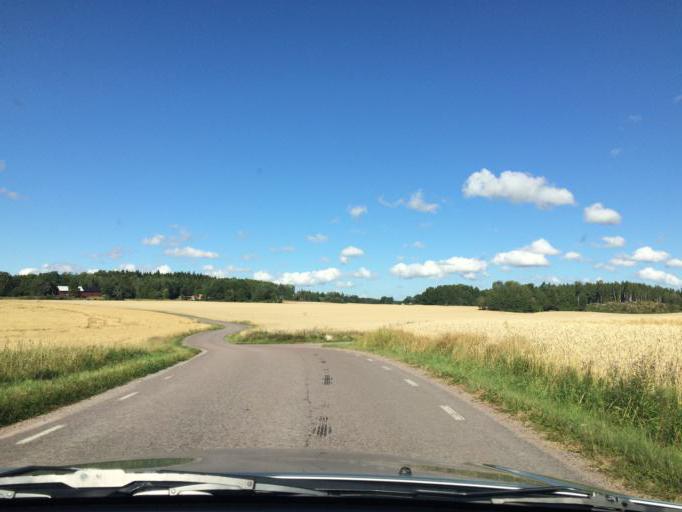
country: SE
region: Soedermanland
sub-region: Eskilstuna Kommun
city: Kvicksund
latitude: 59.5089
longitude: 16.4076
